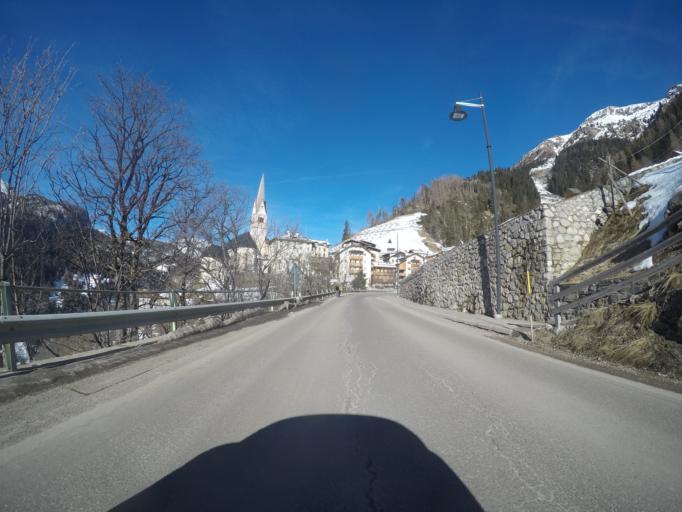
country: IT
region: Veneto
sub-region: Provincia di Belluno
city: Livinallongo del Col di Lana
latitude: 46.4808
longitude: 11.9558
